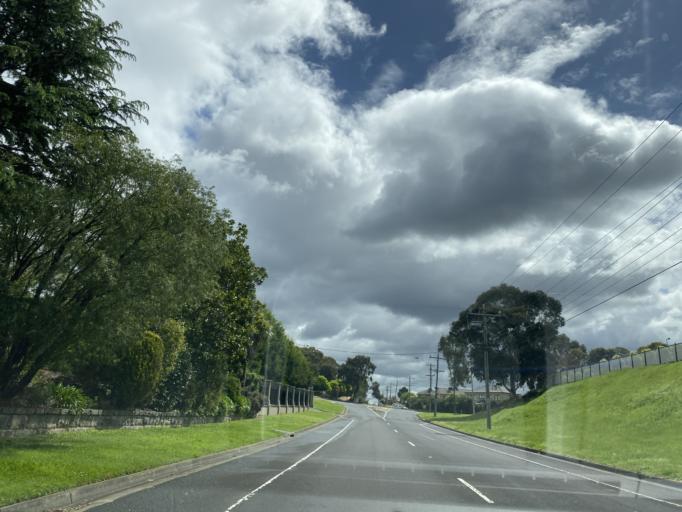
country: AU
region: Victoria
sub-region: Manningham
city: Templestowe Lower
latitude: -37.7617
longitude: 145.1425
